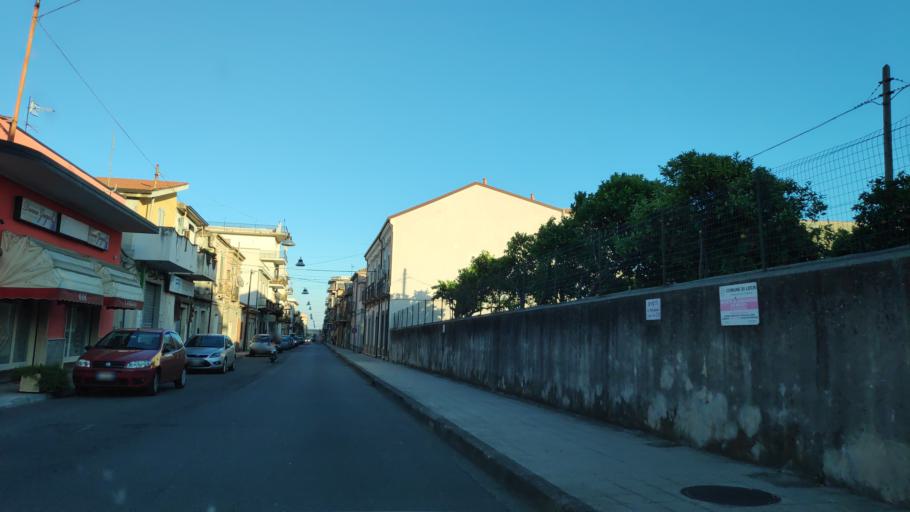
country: IT
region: Calabria
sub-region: Provincia di Reggio Calabria
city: Locri
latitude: 38.2358
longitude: 16.2603
